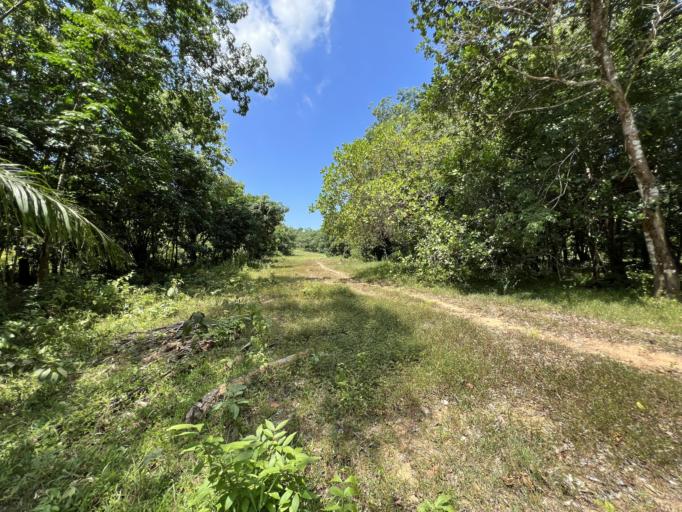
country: MM
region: Tanintharyi
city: Dawei
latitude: 14.5893
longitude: 97.9379
